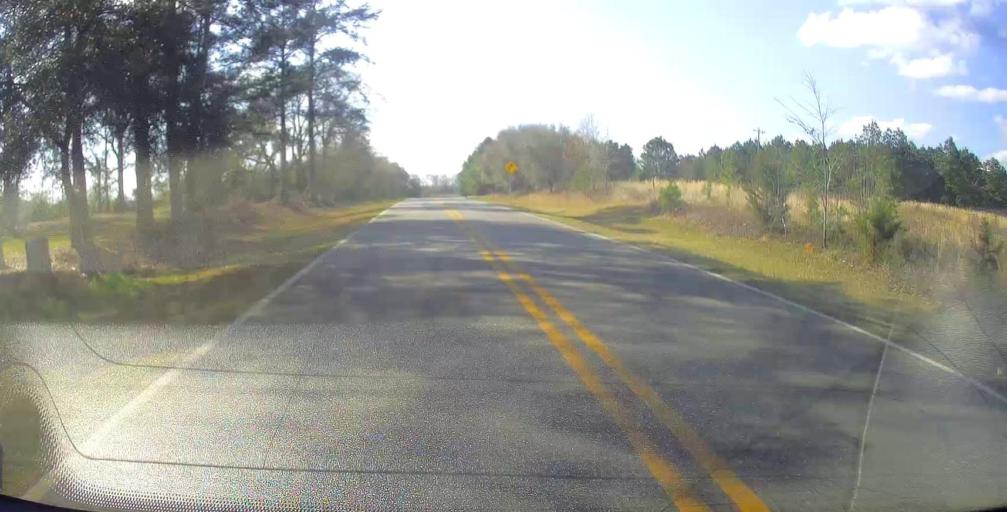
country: US
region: Georgia
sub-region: Laurens County
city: Dublin
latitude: 32.5692
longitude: -83.0365
